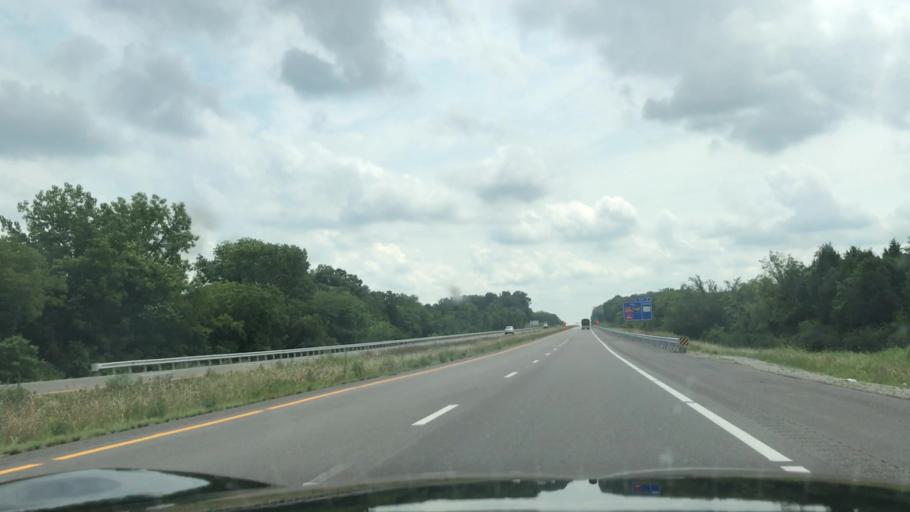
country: US
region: Kentucky
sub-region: Warren County
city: Bowling Green
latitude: 36.9796
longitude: -86.5014
